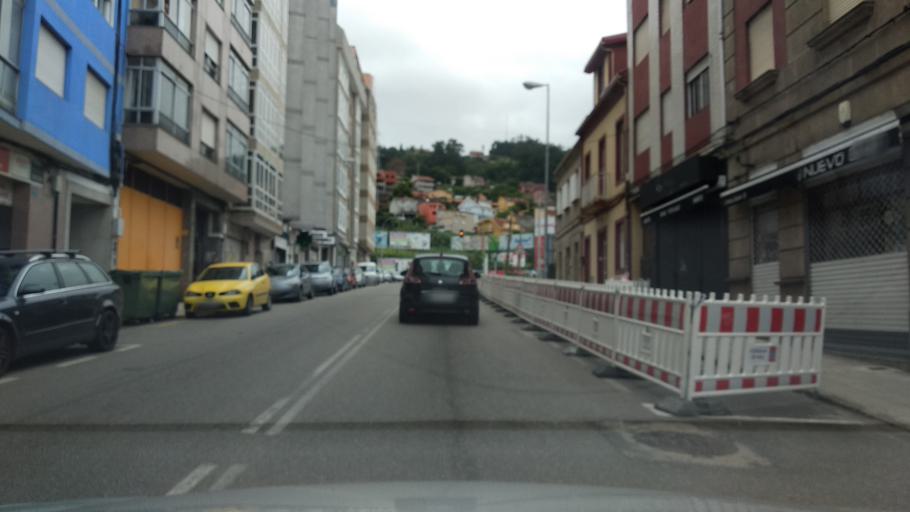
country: ES
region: Galicia
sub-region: Provincia de Pontevedra
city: Vigo
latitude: 42.2474
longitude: -8.6936
